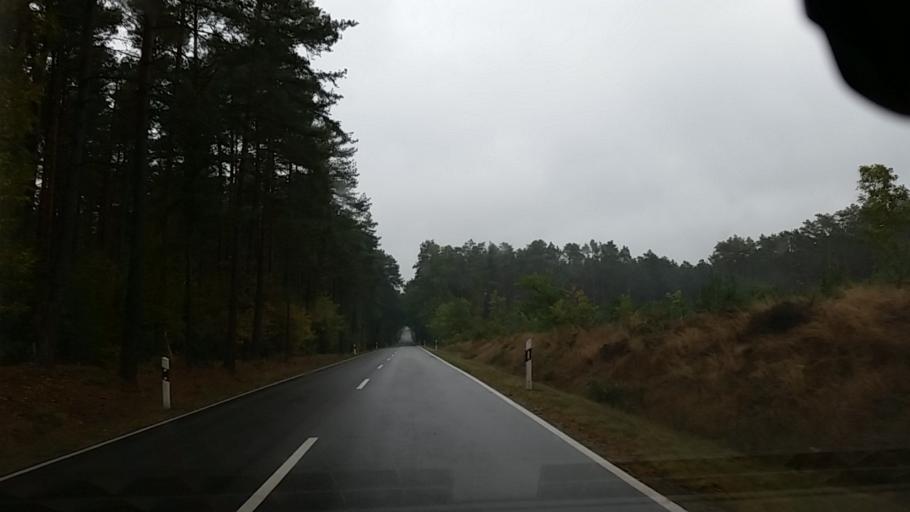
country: DE
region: Lower Saxony
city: Bergfeld
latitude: 52.6100
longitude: 10.8075
